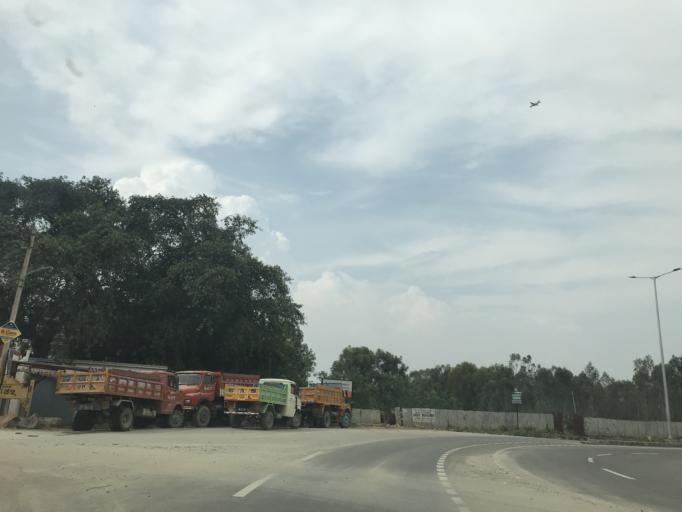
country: IN
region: Karnataka
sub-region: Bangalore Urban
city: Yelahanka
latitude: 13.1061
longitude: 77.6608
